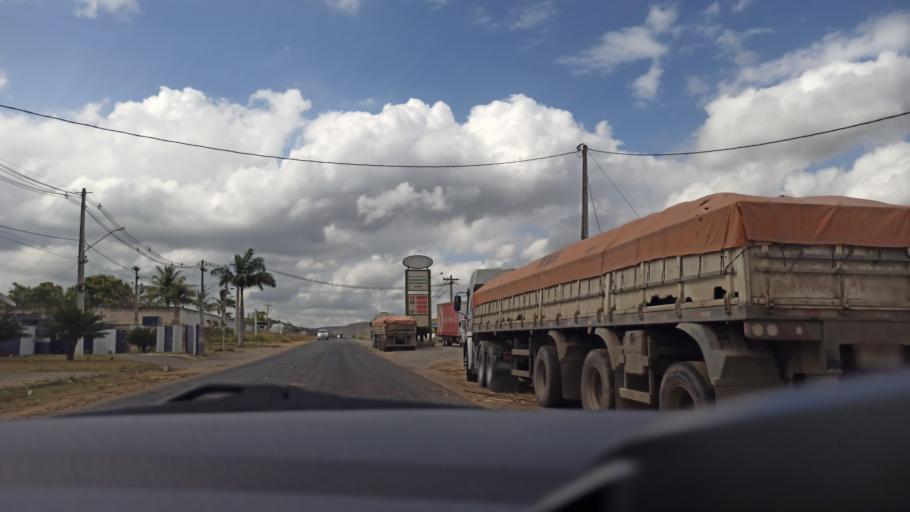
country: BR
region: Pernambuco
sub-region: Timbauba
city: Timbauba
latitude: -7.4950
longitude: -35.2975
